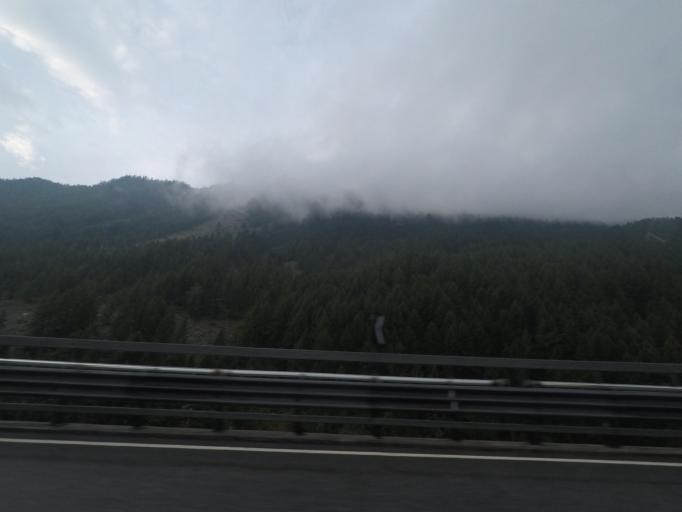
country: IT
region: Aosta Valley
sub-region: Valle d'Aosta
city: San Leonardo
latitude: 45.8198
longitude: 7.1448
